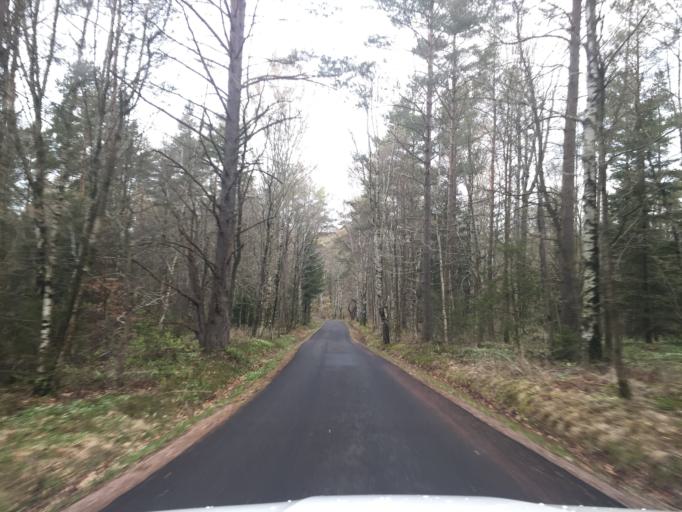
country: SE
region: Vaestra Goetaland
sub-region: Kungalvs Kommun
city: Kungalv
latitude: 57.8459
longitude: 11.9897
